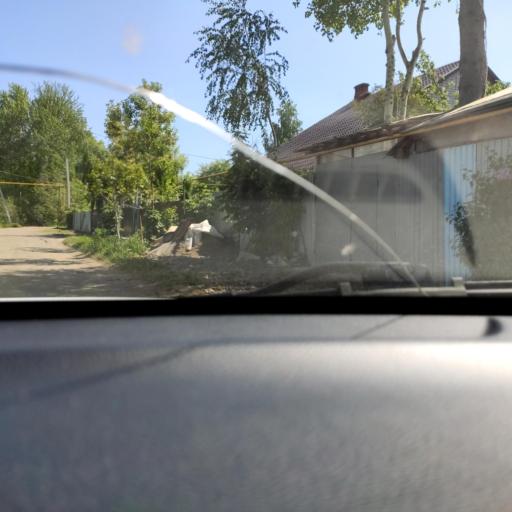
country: RU
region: Tatarstan
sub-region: Gorod Kazan'
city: Kazan
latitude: 55.8593
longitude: 49.1990
